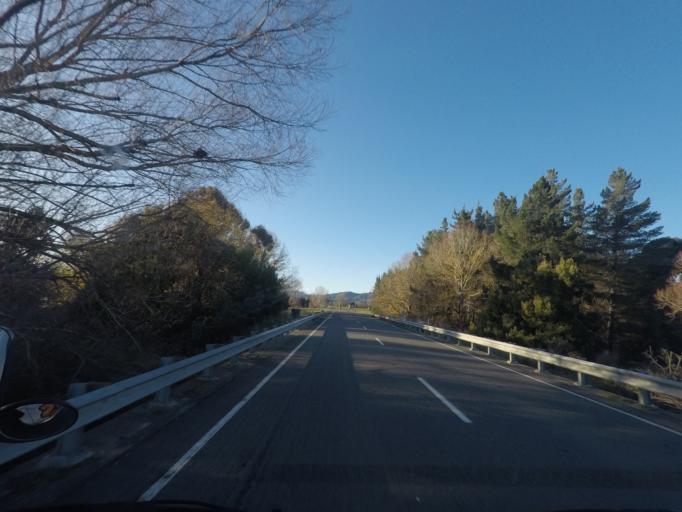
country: NZ
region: Canterbury
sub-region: Kaikoura District
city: Kaikoura
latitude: -42.7198
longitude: 173.2857
